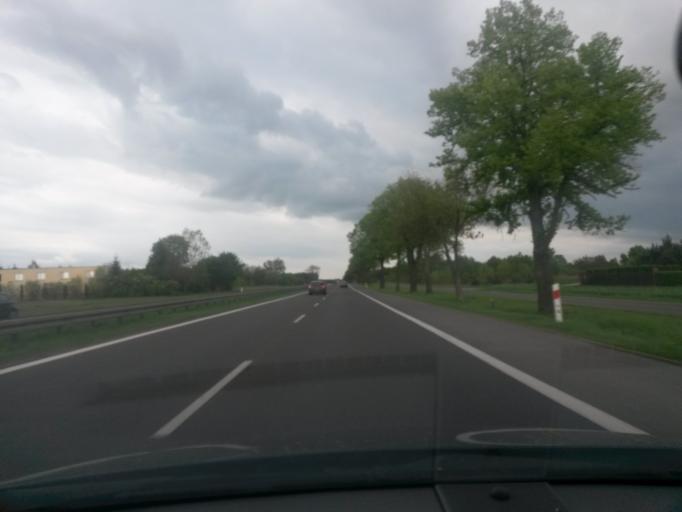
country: PL
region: Masovian Voivodeship
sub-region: Powiat plonski
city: Plonsk
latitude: 52.5851
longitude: 20.4591
